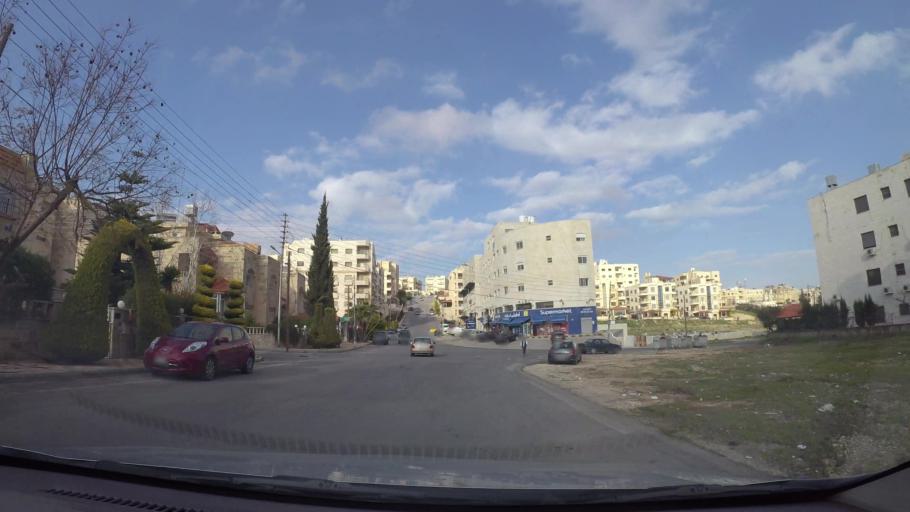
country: JO
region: Amman
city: Al Jubayhah
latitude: 31.9857
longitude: 35.8544
